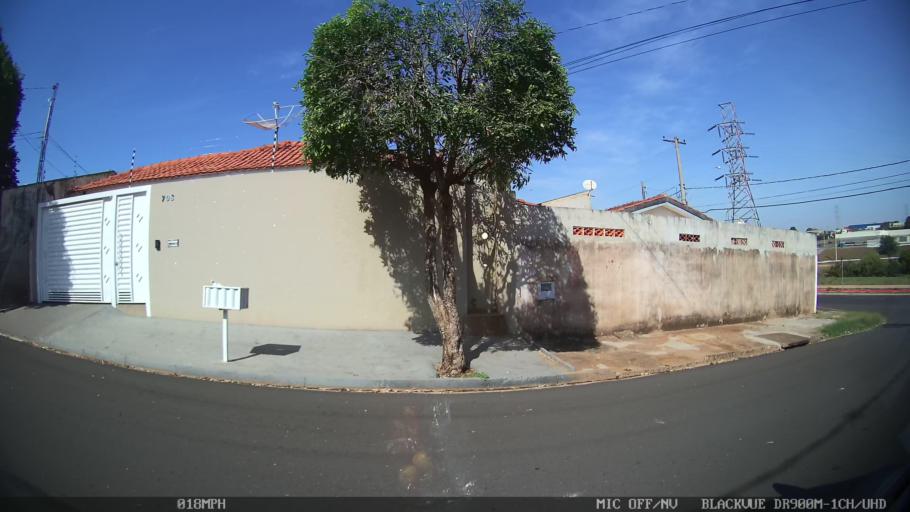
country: BR
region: Sao Paulo
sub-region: Sao Jose Do Rio Preto
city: Sao Jose do Rio Preto
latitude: -20.7882
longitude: -49.4131
